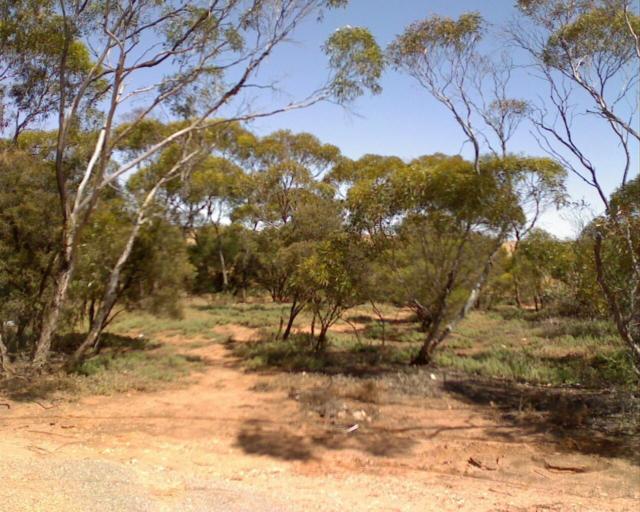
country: AU
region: South Australia
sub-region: Kimba
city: Caralue
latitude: -33.1465
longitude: 135.7557
